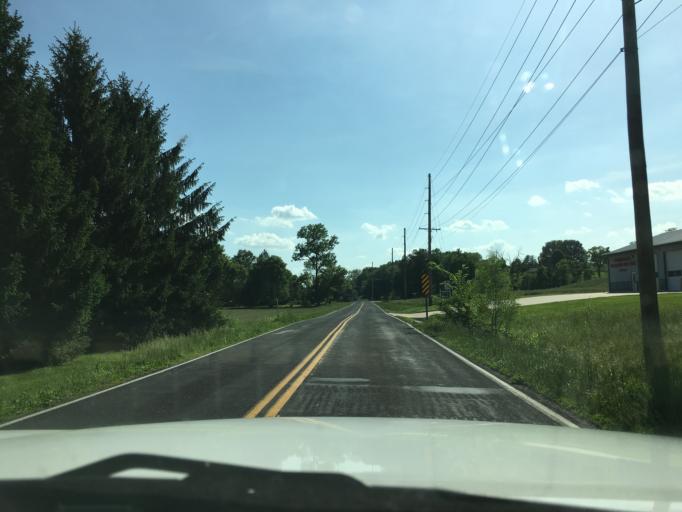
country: US
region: Missouri
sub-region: Franklin County
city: Washington
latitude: 38.6093
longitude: -90.9881
